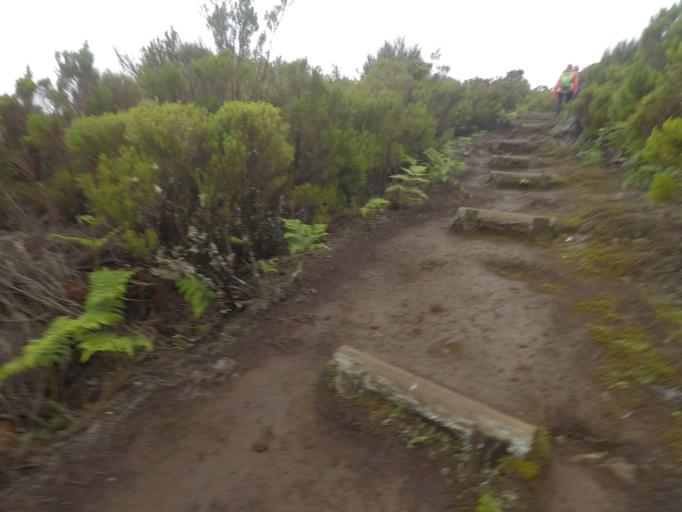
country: PT
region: Madeira
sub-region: Calheta
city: Arco da Calheta
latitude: 32.7730
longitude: -17.1269
